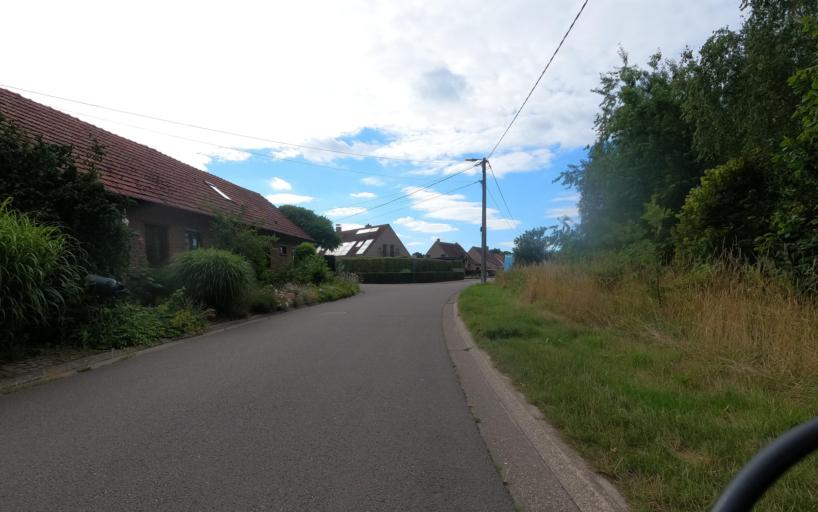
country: BE
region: Flanders
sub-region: Provincie Vlaams-Brabant
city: Begijnendijk
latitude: 51.0174
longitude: 4.7520
